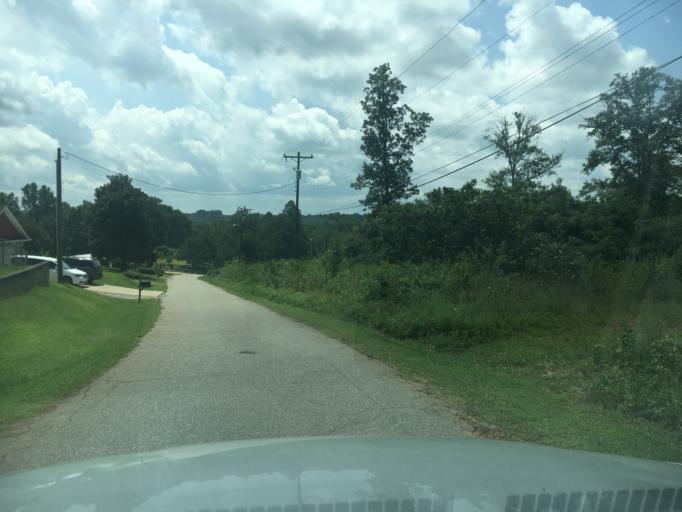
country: US
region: South Carolina
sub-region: Spartanburg County
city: Duncan
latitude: 34.9332
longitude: -82.1386
